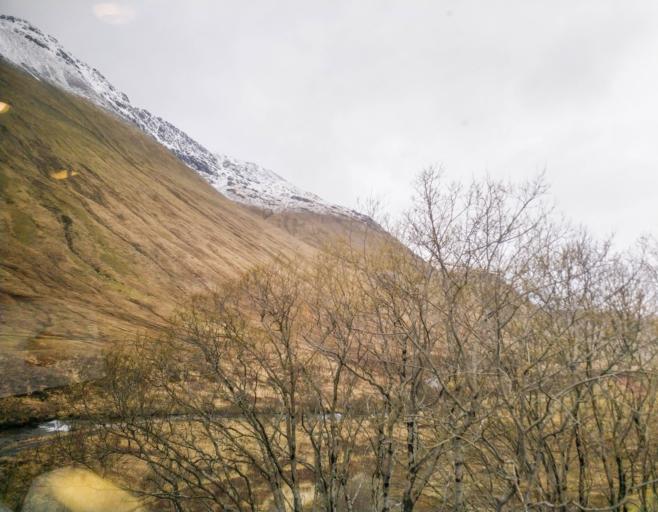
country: GB
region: Scotland
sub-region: Argyll and Bute
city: Garelochhead
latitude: 56.4887
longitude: -4.7044
